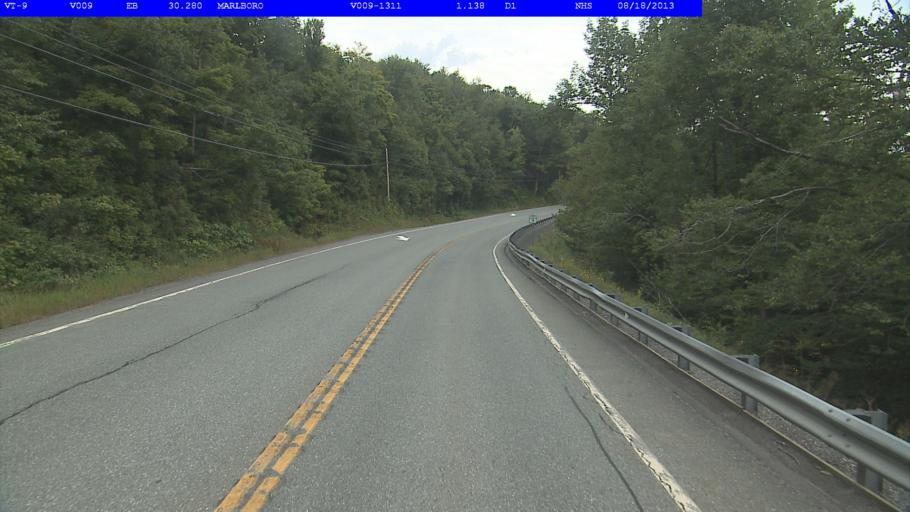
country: US
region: Vermont
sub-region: Windham County
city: Dover
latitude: 42.8580
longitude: -72.7885
